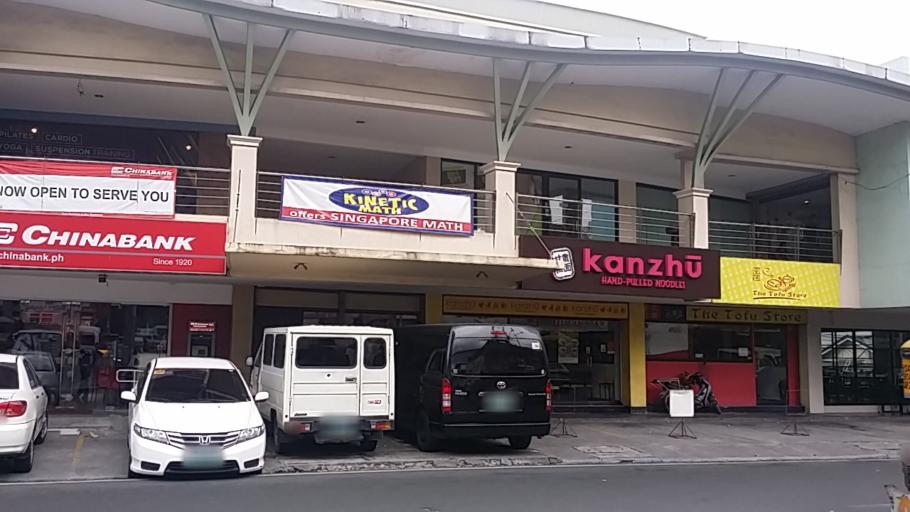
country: PH
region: Metro Manila
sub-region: San Juan
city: San Juan
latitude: 14.5984
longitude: 121.0383
